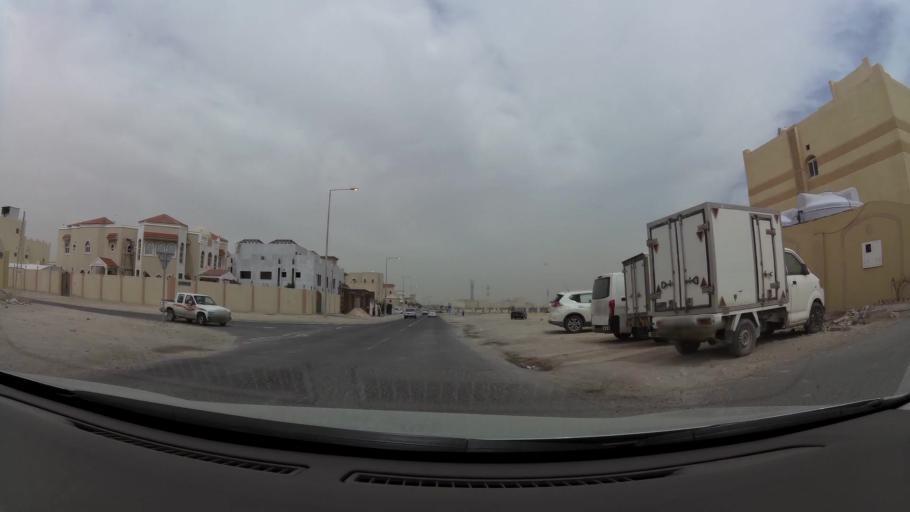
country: QA
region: Baladiyat ar Rayyan
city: Ar Rayyan
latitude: 25.2238
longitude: 51.4605
